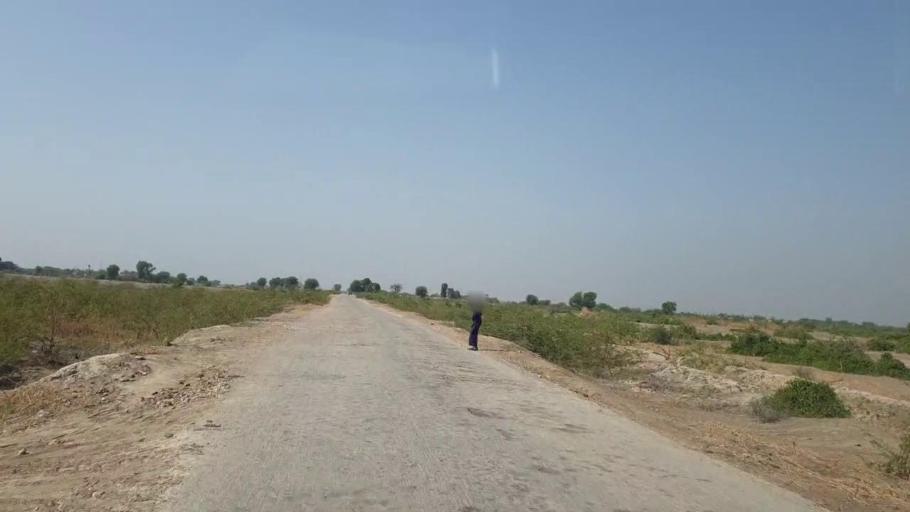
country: PK
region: Sindh
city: Naukot
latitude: 25.0175
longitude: 69.4682
